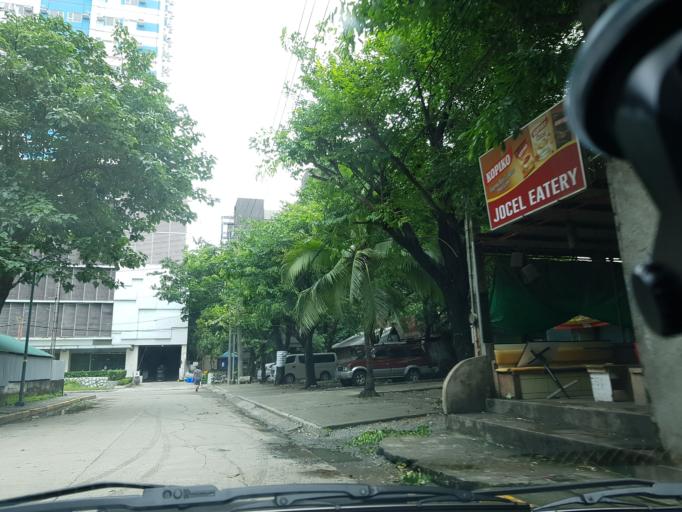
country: PH
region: Metro Manila
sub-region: Pasig
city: Pasig City
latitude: 14.5783
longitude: 121.0593
